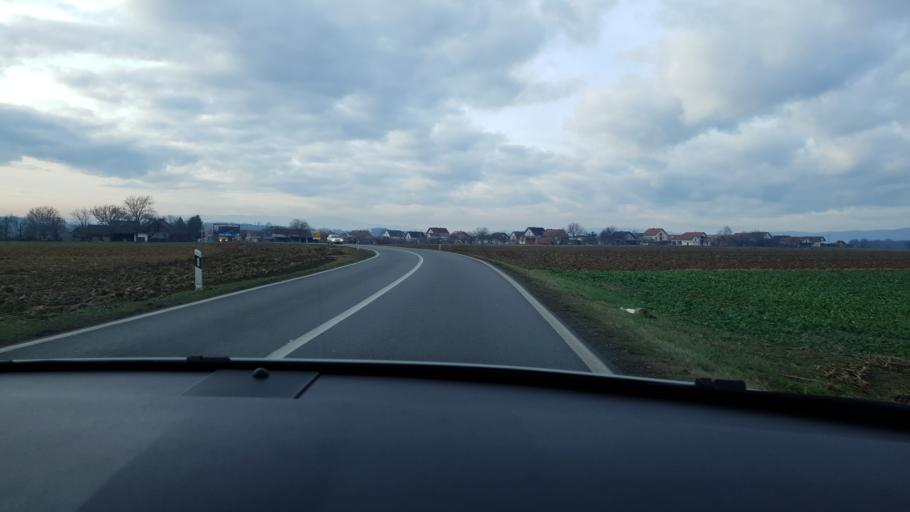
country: HR
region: Pozesko-Slavonska
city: Jaksic
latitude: 45.3574
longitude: 17.7434
